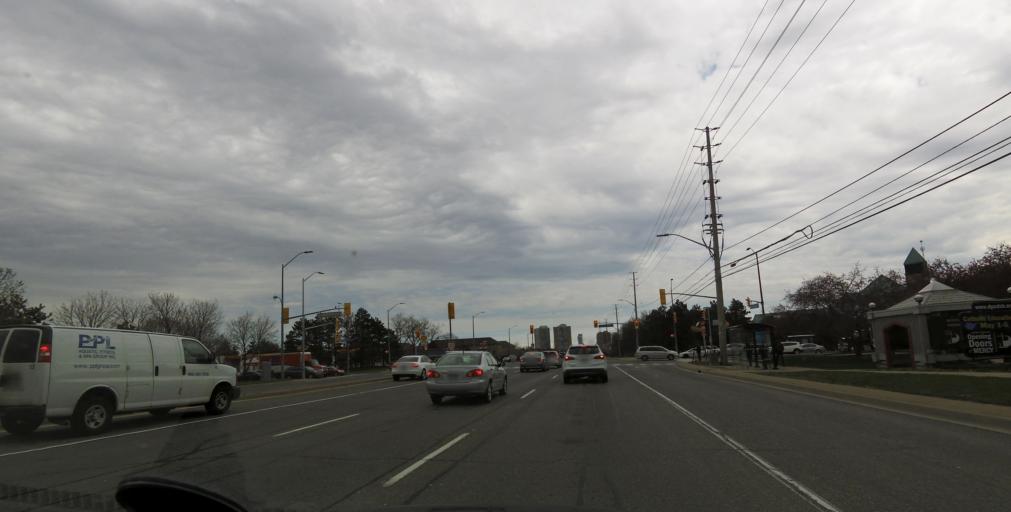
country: CA
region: Ontario
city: Mississauga
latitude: 43.6198
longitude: -79.6709
